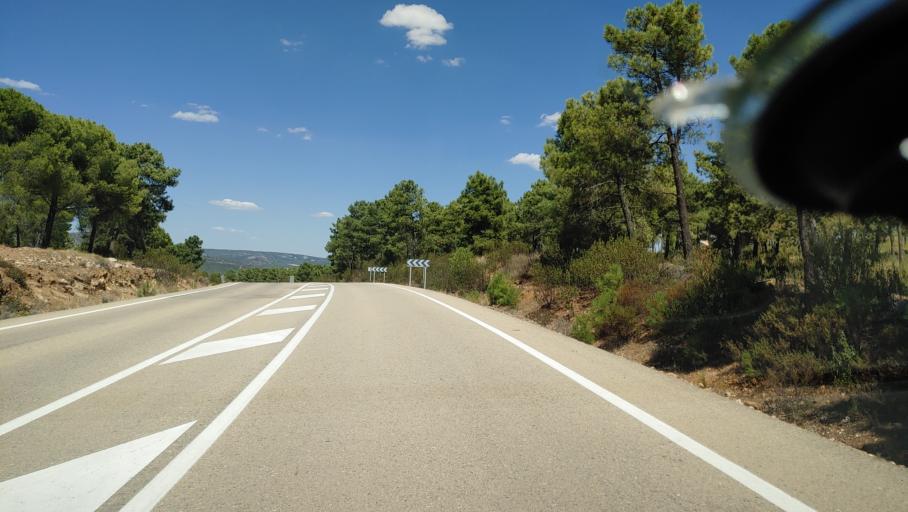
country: ES
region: Castille-La Mancha
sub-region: Provincia de Ciudad Real
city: Saceruela
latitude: 39.0002
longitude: -4.5145
